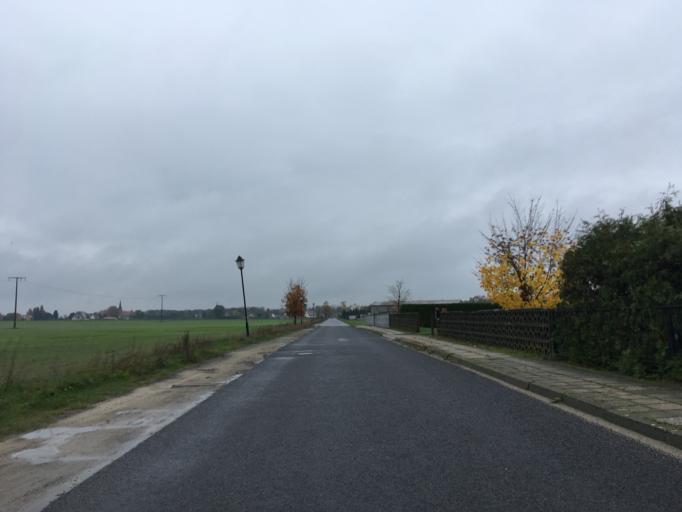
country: DE
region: Brandenburg
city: Tauche
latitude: 52.0768
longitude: 14.1791
